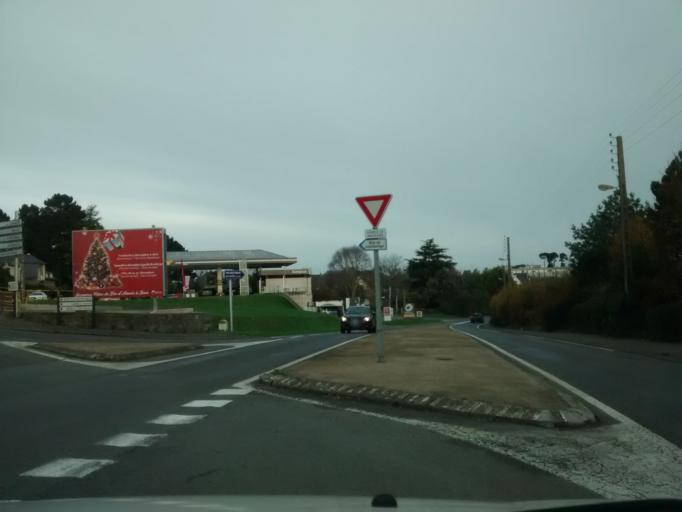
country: FR
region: Brittany
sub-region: Departement d'Ille-et-Vilaine
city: Dinard
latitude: 48.6207
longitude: -2.0578
